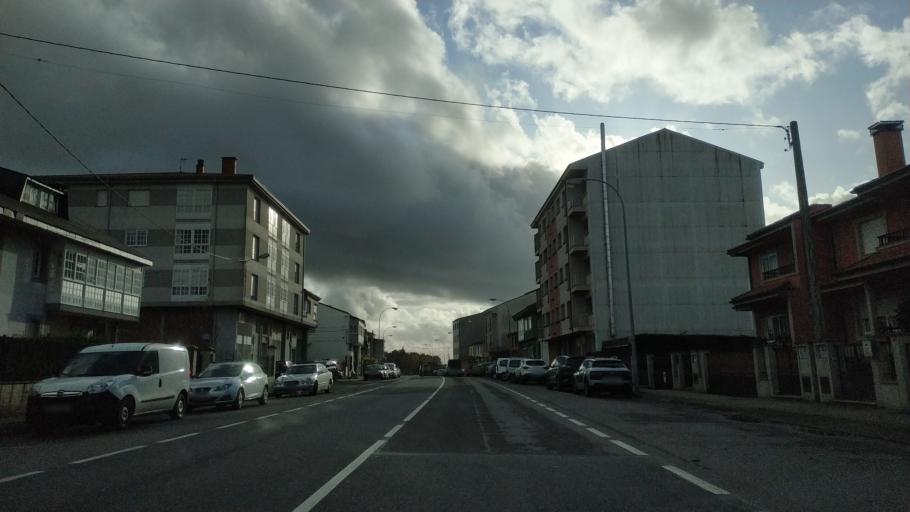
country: ES
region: Galicia
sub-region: Provincia da Coruna
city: Arzua
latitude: 42.9368
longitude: -8.1606
